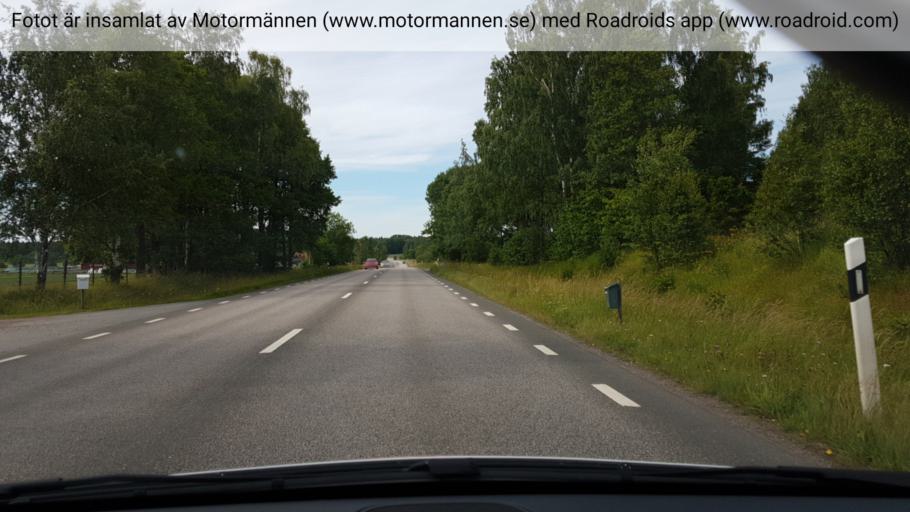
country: SE
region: Vaestra Goetaland
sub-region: Hjo Kommun
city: Hjo
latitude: 58.3274
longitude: 14.2583
